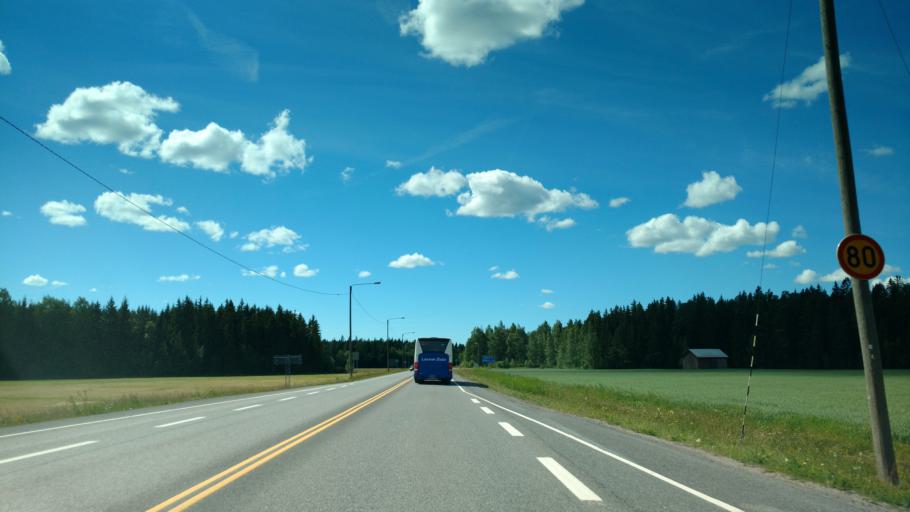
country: FI
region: Varsinais-Suomi
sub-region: Turku
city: Kaarina
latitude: 60.4653
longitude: 22.4020
